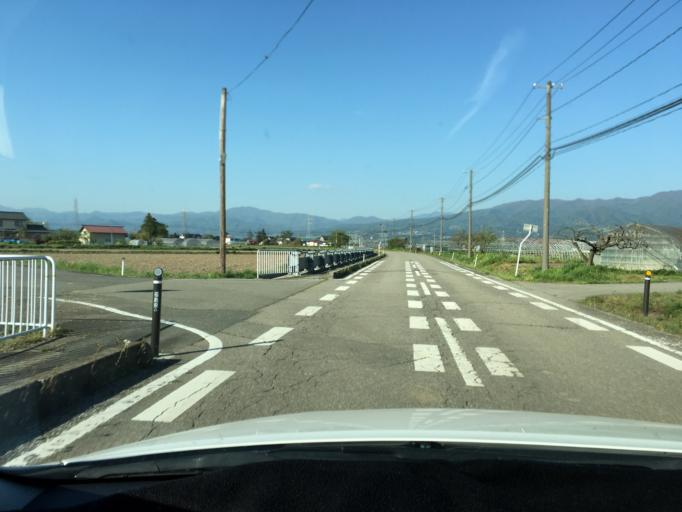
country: JP
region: Fukushima
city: Kitakata
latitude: 37.5705
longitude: 139.8744
